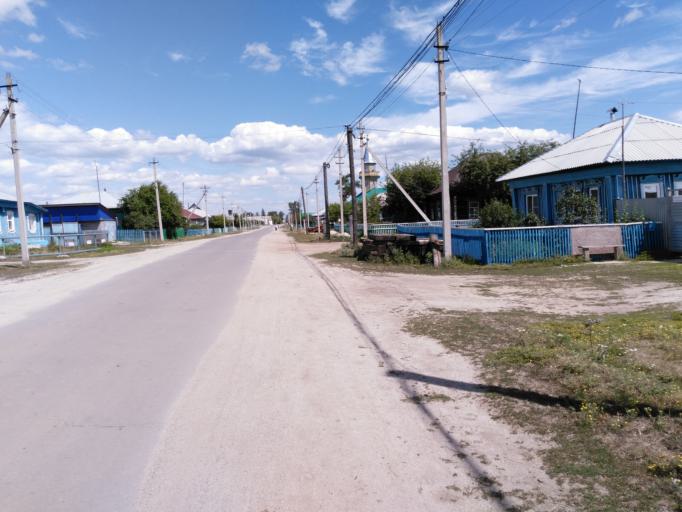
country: RU
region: Bashkortostan
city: Akhunovo
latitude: 54.2051
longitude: 59.5927
